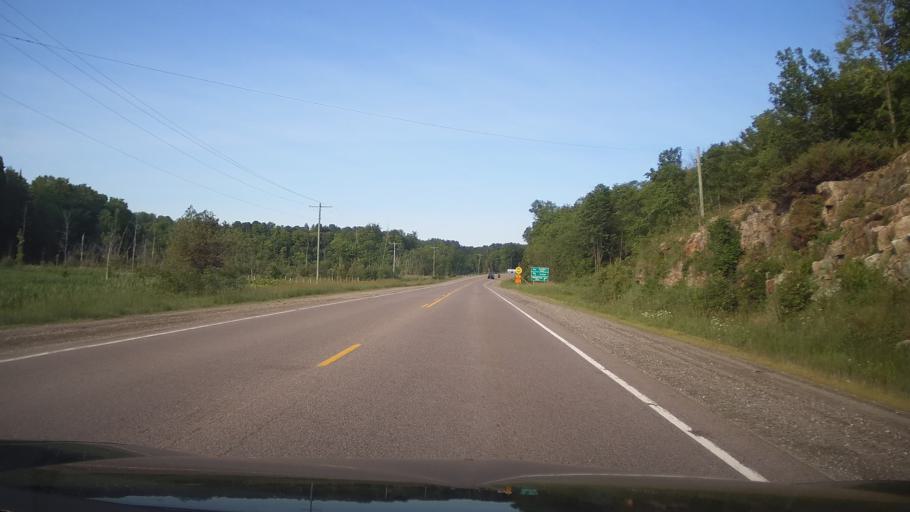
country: CA
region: Ontario
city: Skatepark
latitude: 44.7432
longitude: -76.9237
